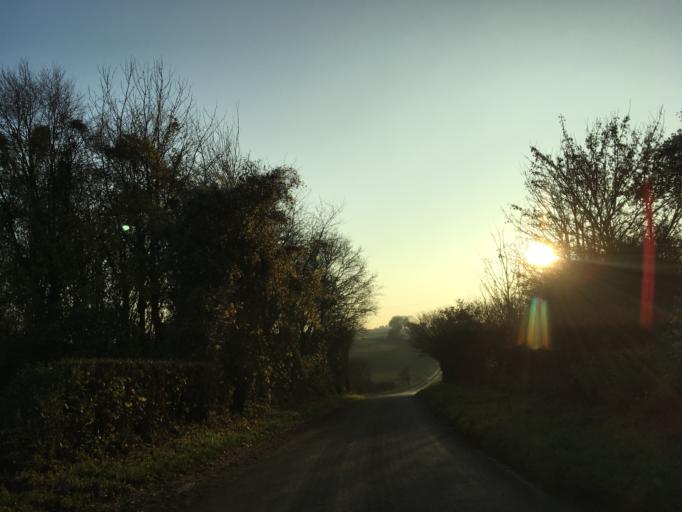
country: GB
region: England
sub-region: Wiltshire
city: Nettleton
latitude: 51.4840
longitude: -2.2626
